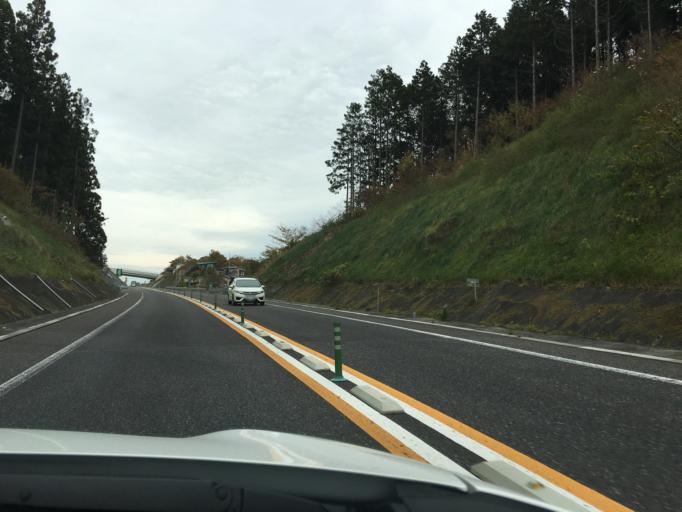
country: JP
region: Fukushima
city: Ishikawa
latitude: 37.2127
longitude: 140.5404
